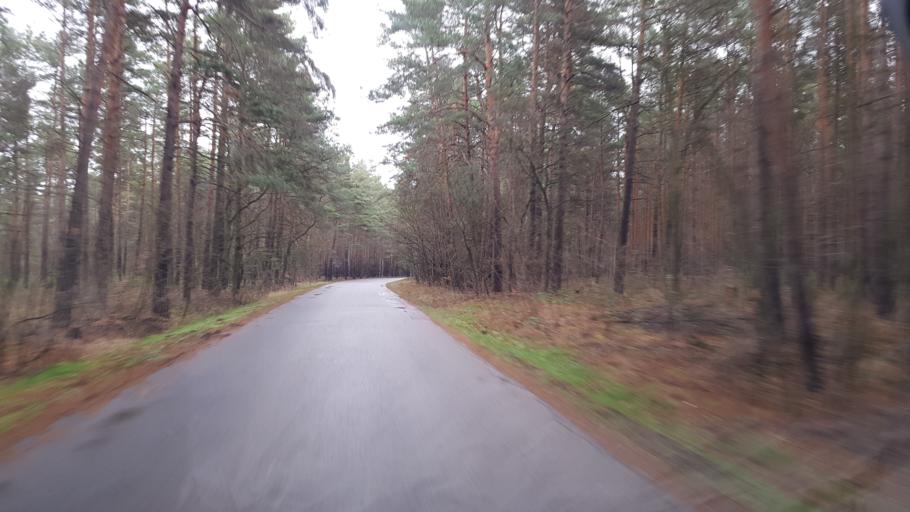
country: DE
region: Brandenburg
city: Calau
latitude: 51.7212
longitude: 14.0032
